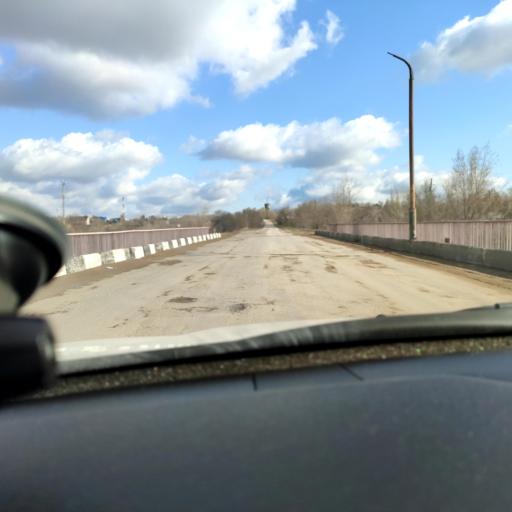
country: RU
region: Samara
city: Smyshlyayevka
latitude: 53.2413
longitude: 50.4809
